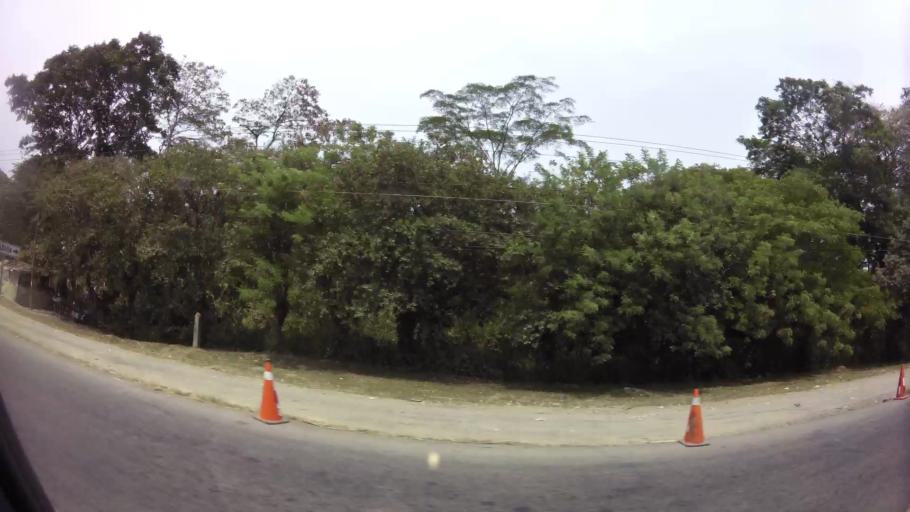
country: HN
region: Cortes
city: Nuevo Chamelecon
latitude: 15.3704
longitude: -87.9857
